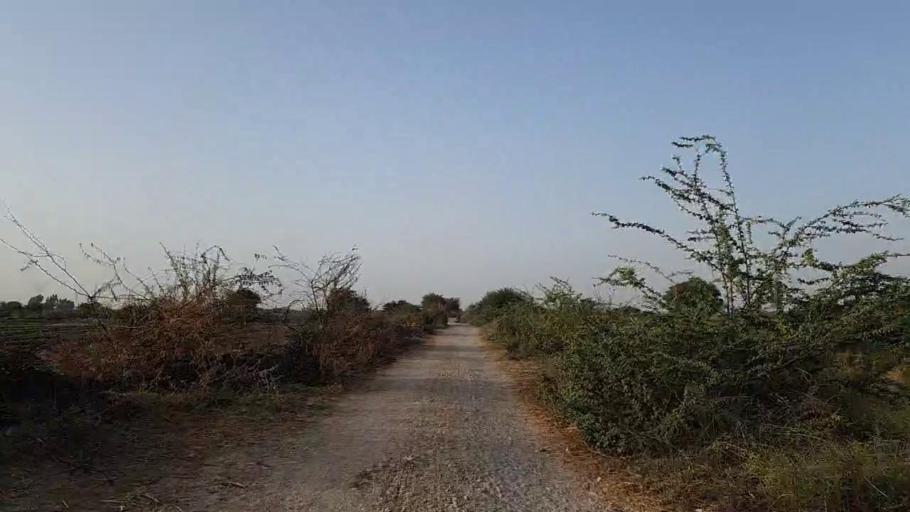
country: PK
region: Sindh
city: Jati
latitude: 24.4086
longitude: 68.1858
